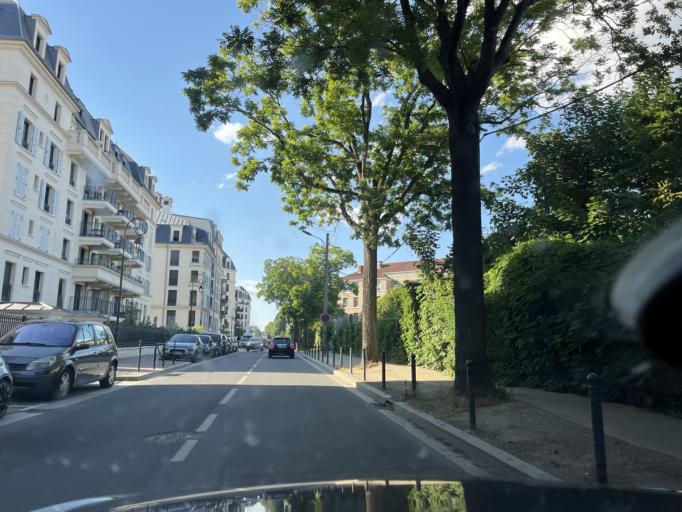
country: FR
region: Ile-de-France
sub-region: Departement des Hauts-de-Seine
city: Le Plessis-Robinson
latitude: 48.7916
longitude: 2.2728
